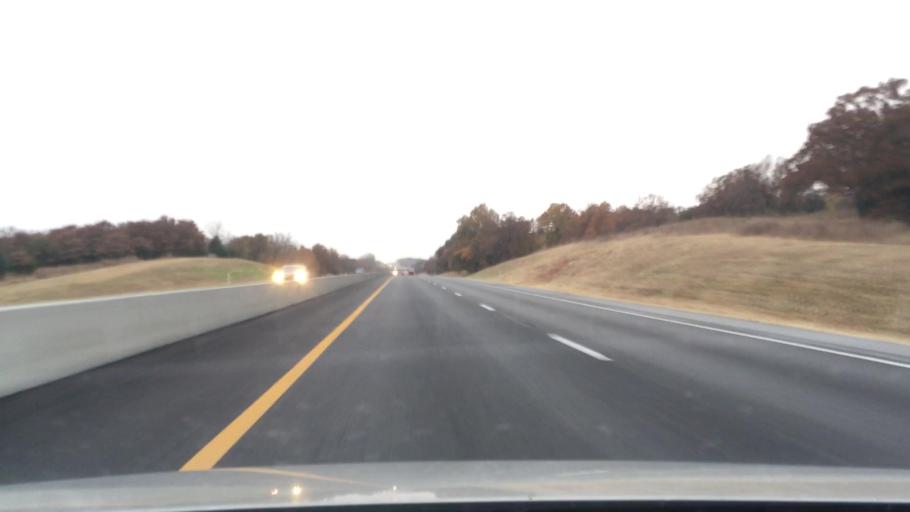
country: US
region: Oklahoma
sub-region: Lincoln County
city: Stroud
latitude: 35.7422
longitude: -96.7518
